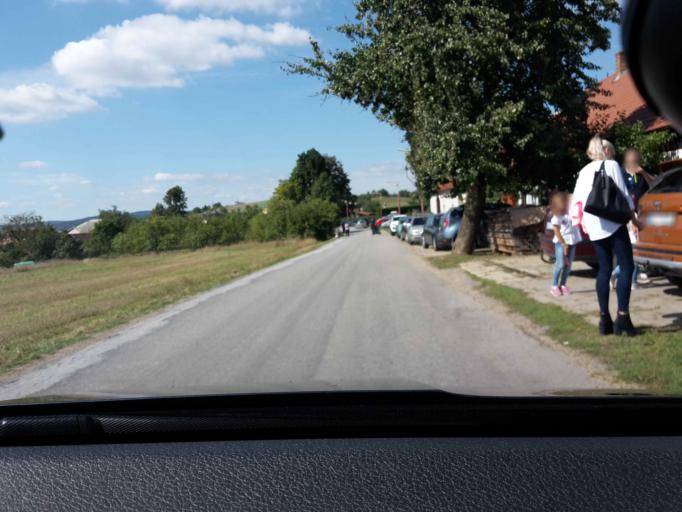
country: CZ
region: Vysocina
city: Zeletava
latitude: 49.1189
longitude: 15.6205
